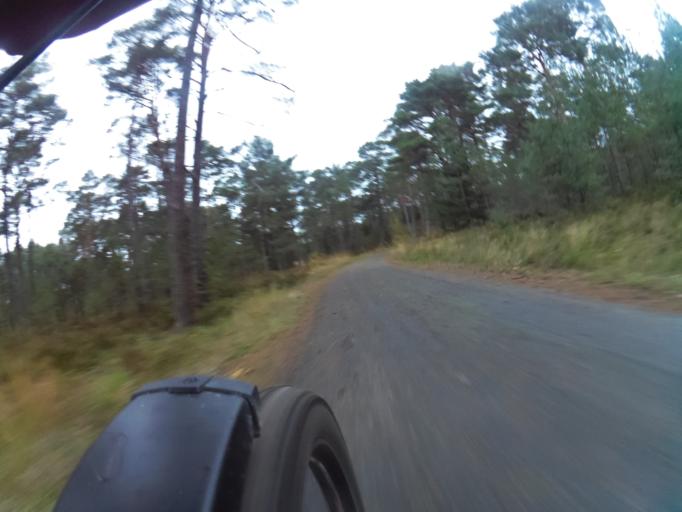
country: PL
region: Pomeranian Voivodeship
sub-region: Powiat wejherowski
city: Choczewo
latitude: 54.7929
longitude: 17.7596
